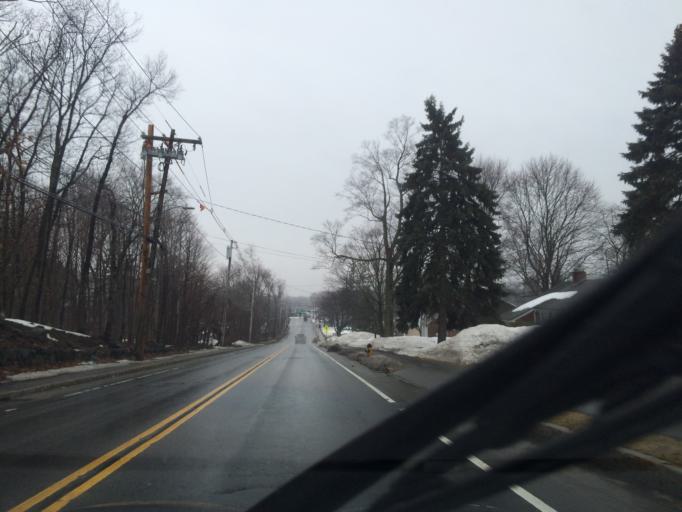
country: US
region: Massachusetts
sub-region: Middlesex County
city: Waltham
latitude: 42.4036
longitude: -71.2162
